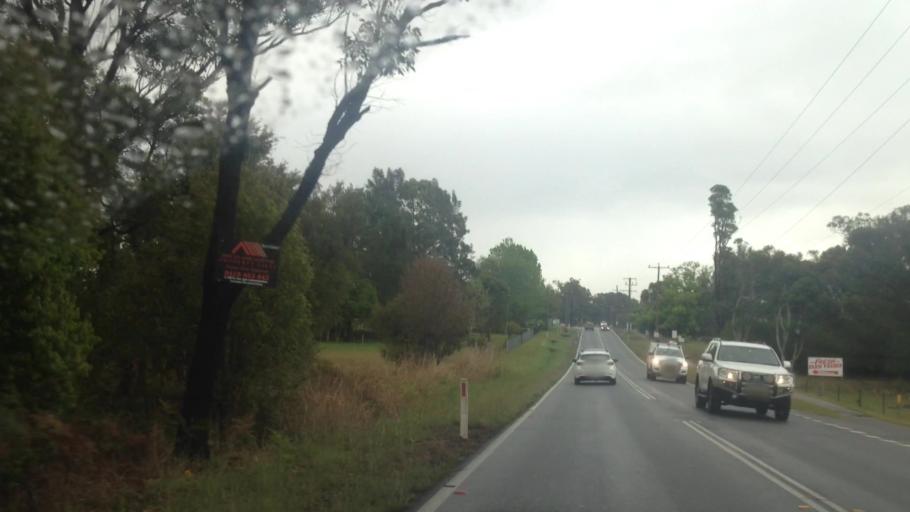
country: AU
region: New South Wales
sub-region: Wyong Shire
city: Charmhaven
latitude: -33.1720
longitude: 151.4781
